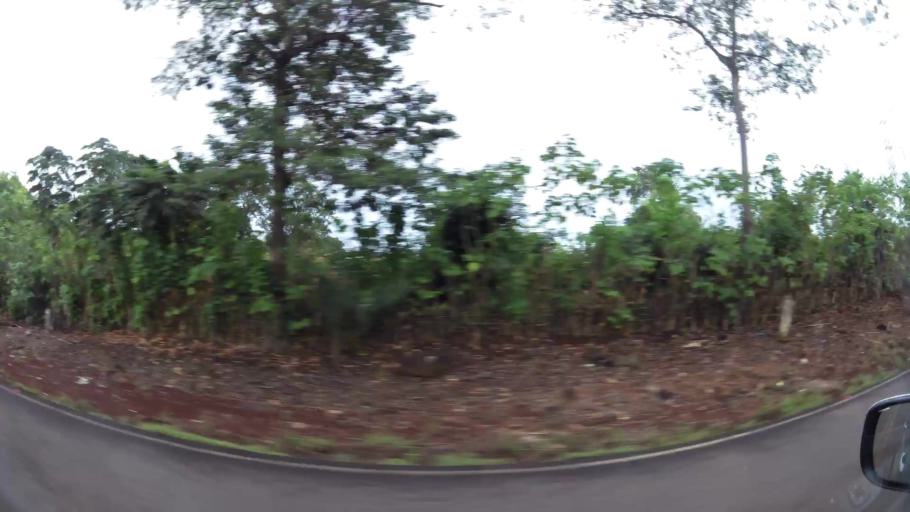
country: CR
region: Puntarenas
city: Esparza
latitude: 9.9707
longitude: -84.6164
